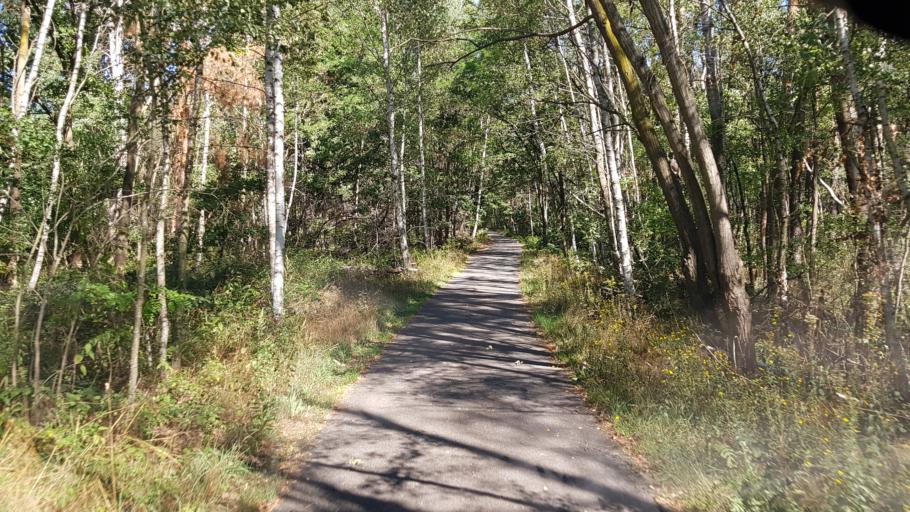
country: DE
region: Brandenburg
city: Altdobern
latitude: 51.6991
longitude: 13.9994
